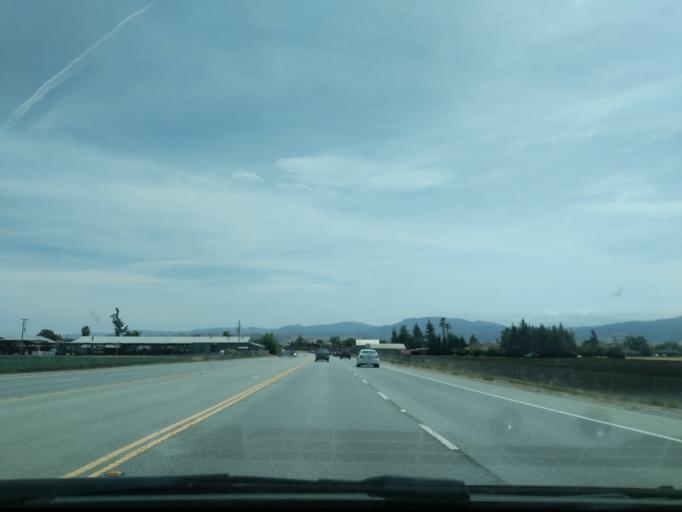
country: US
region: California
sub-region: San Benito County
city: Hollister
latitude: 36.8594
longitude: -121.3908
